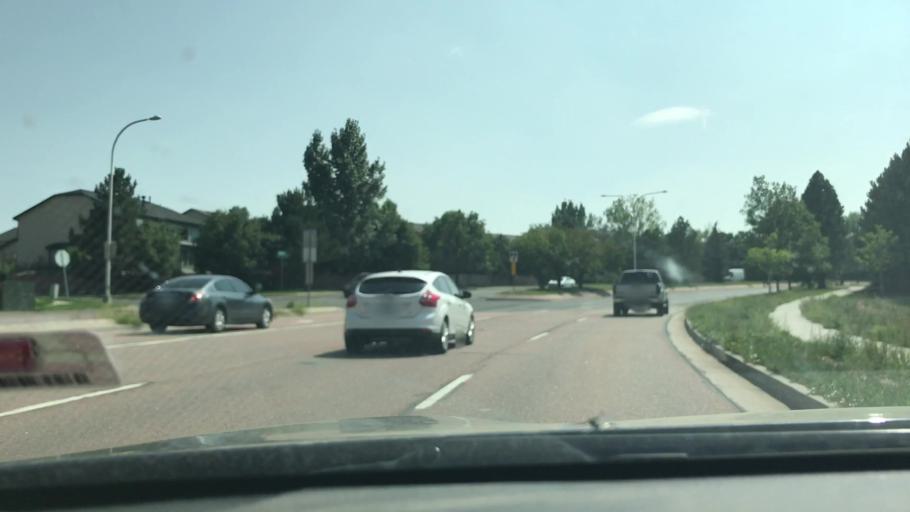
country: US
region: Colorado
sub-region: El Paso County
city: Black Forest
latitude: 38.9628
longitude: -104.7579
